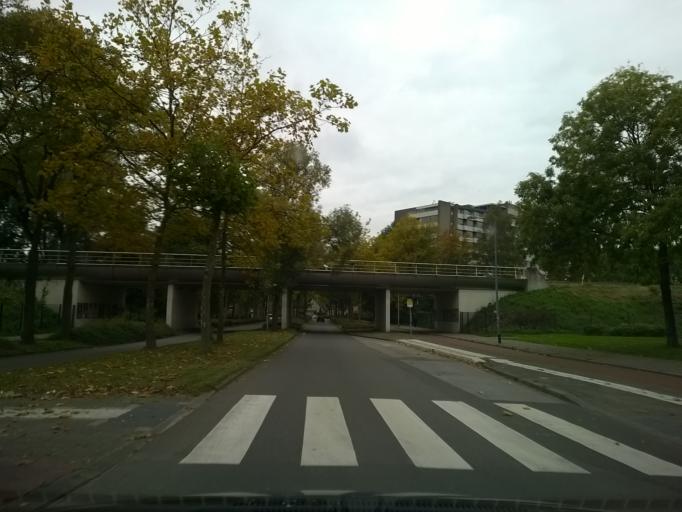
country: NL
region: Groningen
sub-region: Gemeente Groningen
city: Korrewegwijk
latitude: 53.2329
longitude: 6.5591
